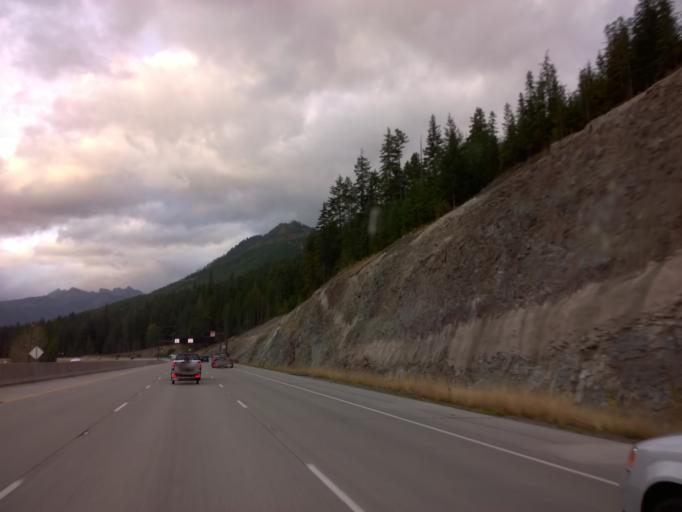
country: US
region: Washington
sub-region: King County
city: Tanner
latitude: 47.3644
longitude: -121.3727
